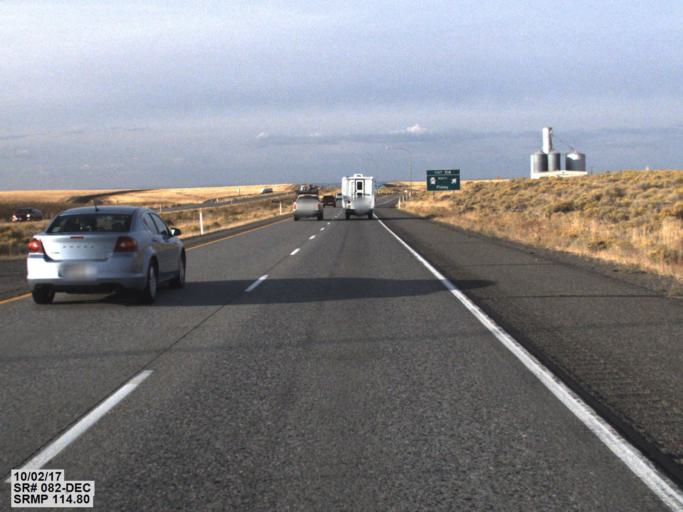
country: US
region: Washington
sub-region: Benton County
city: Highland
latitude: 46.1365
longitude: -119.2019
